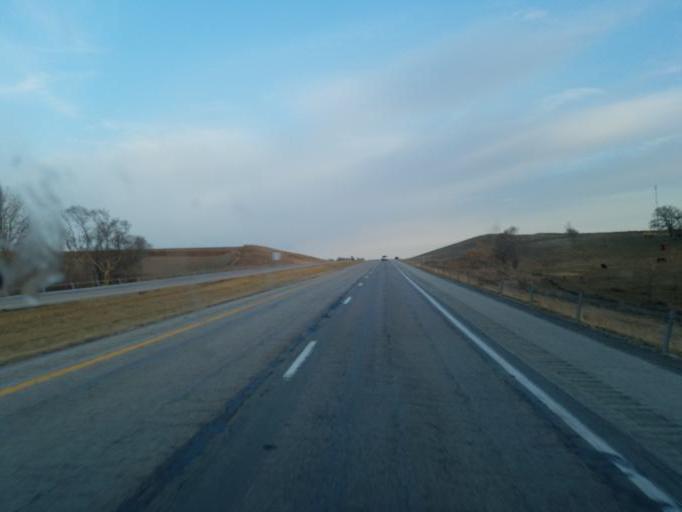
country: US
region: Iowa
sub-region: Harrison County
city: Missouri Valley
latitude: 41.4996
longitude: -95.7859
